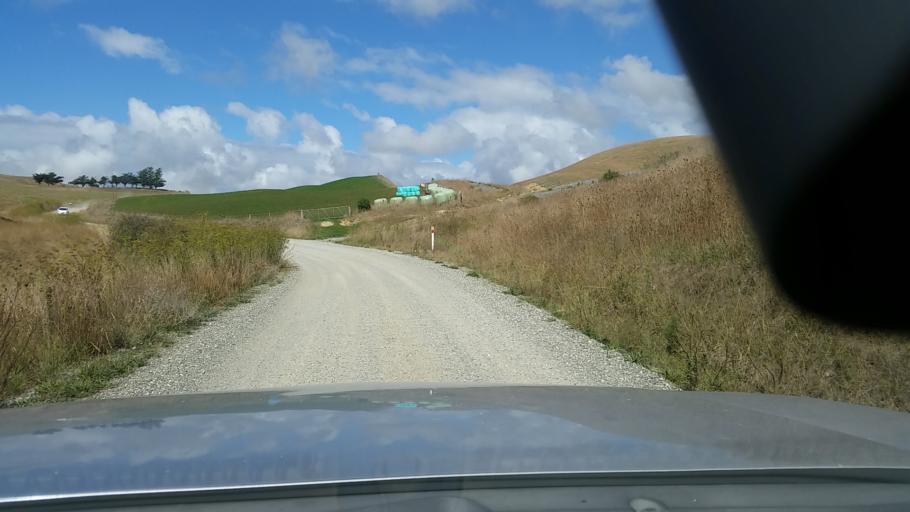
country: NZ
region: Marlborough
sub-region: Marlborough District
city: Blenheim
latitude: -41.6926
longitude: 174.1438
